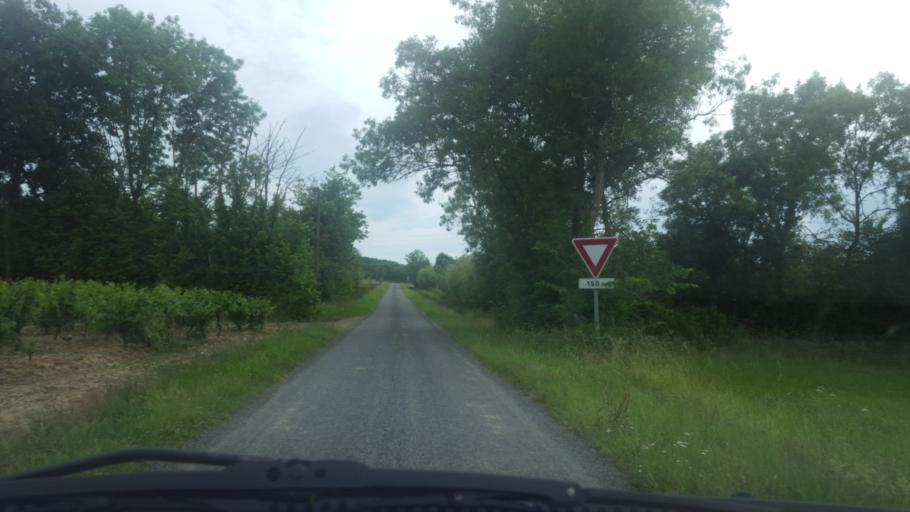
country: FR
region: Pays de la Loire
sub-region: Departement de la Loire-Atlantique
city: La Limouziniere
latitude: 47.0243
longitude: -1.6064
